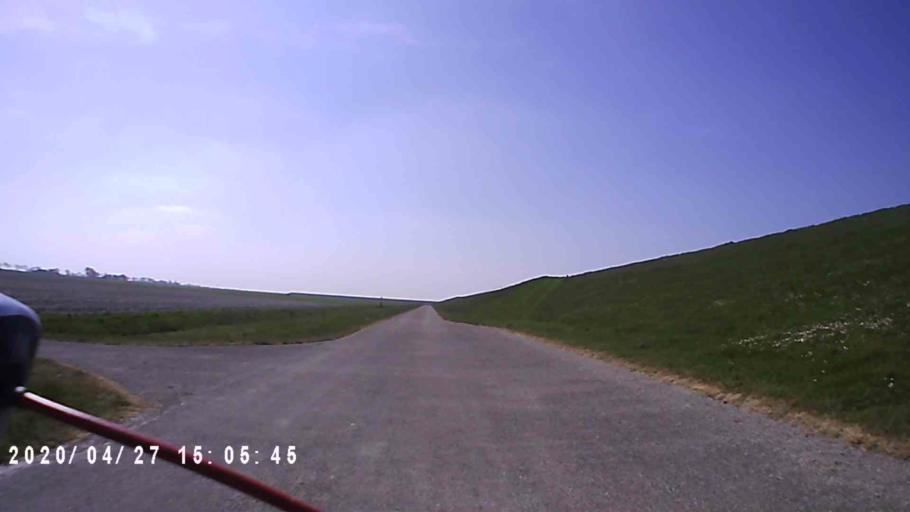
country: NL
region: Groningen
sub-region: Gemeente Winsum
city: Winsum
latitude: 53.4218
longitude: 6.4565
